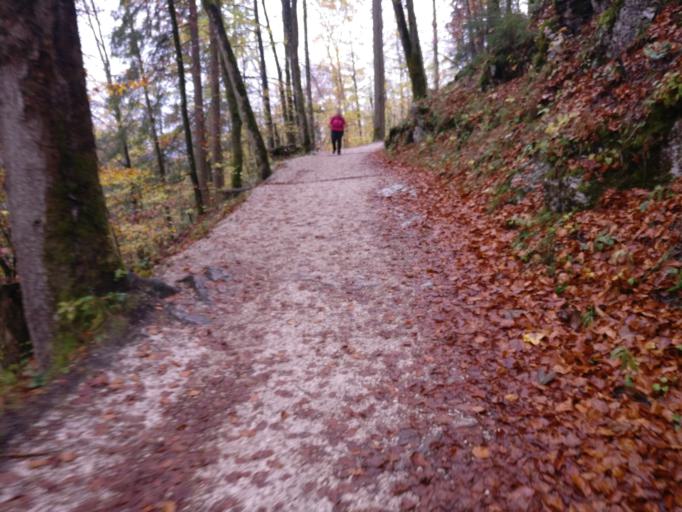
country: DE
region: Bavaria
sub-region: Upper Bavaria
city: Schoenau am Koenigssee
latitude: 47.5835
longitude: 12.9913
